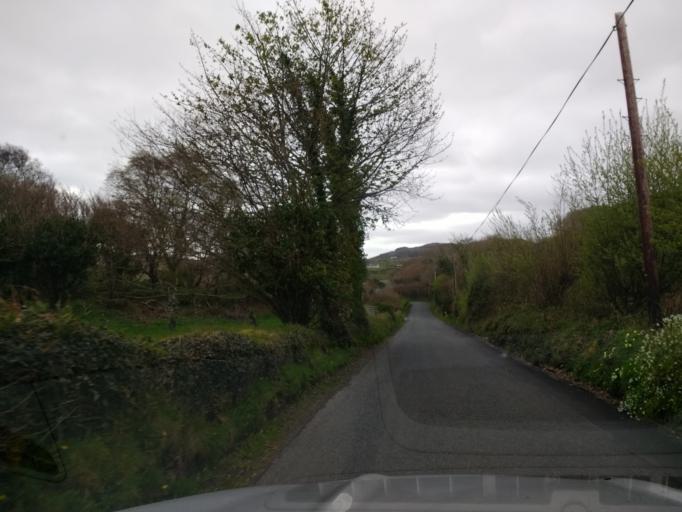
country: IE
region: Ulster
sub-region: County Donegal
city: Buncrana
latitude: 55.2350
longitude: -7.6182
